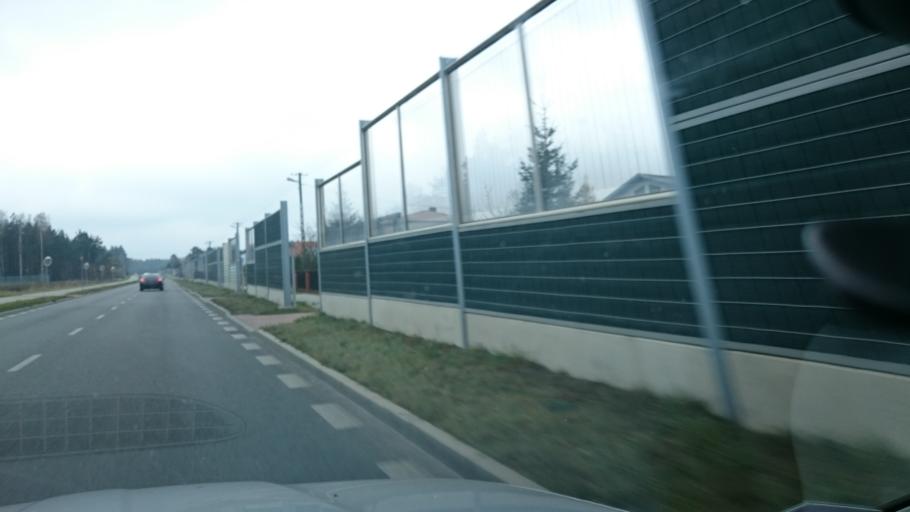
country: PL
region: Swietokrzyskie
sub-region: Powiat konecki
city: Konskie
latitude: 51.1578
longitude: 20.3666
